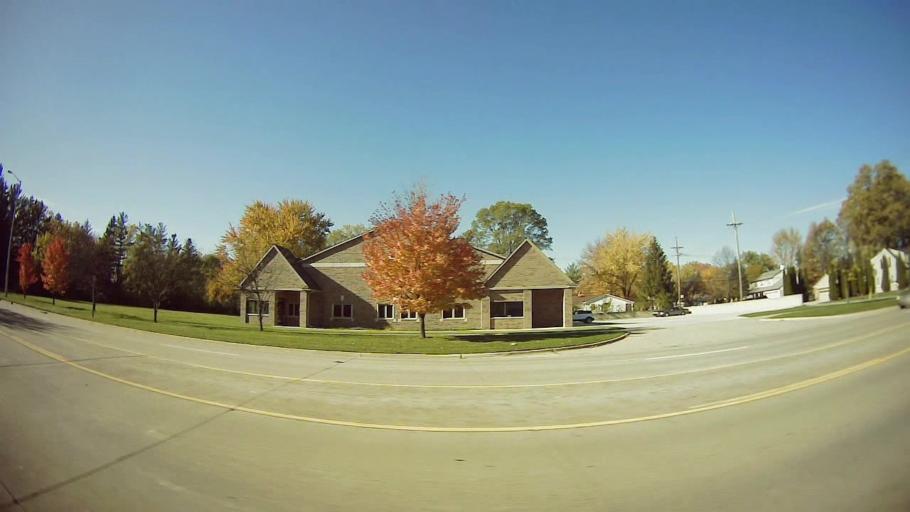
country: US
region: Michigan
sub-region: Oakland County
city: Farmington
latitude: 42.4507
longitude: -83.3756
